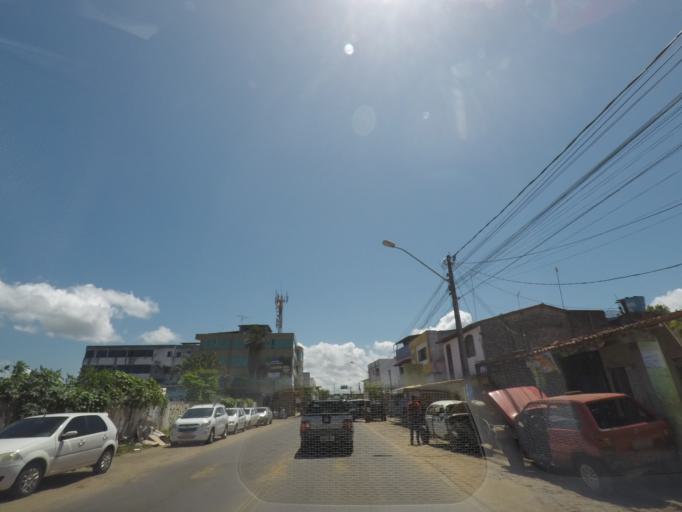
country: BR
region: Bahia
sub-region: Valenca
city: Valenca
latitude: -13.3592
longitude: -39.0657
